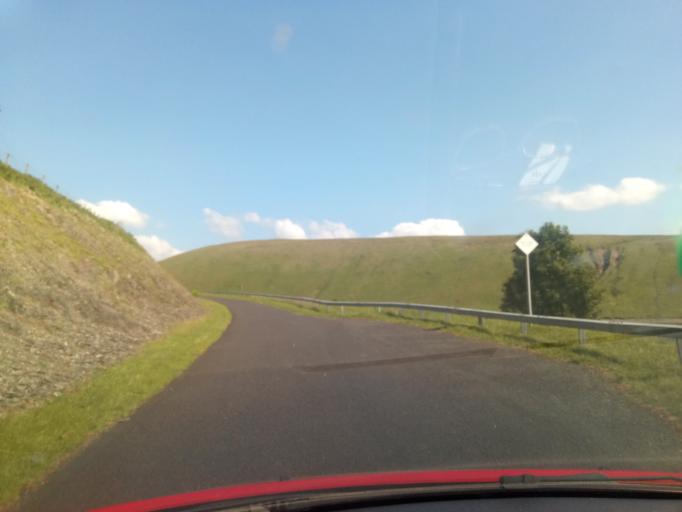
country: GB
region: Scotland
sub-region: The Scottish Borders
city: Peebles
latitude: 55.4938
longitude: -3.2708
